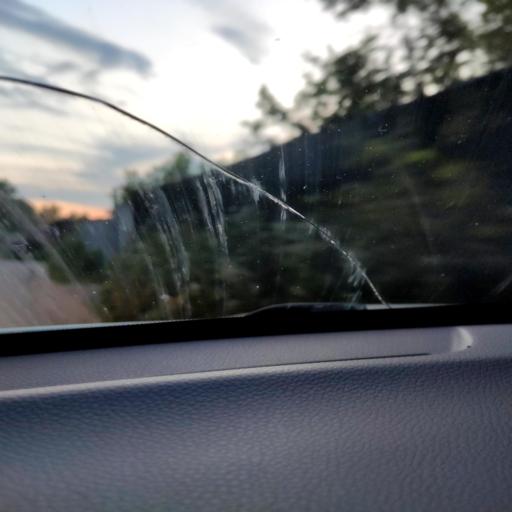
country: RU
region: Tatarstan
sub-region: Gorod Kazan'
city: Kazan
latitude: 55.8472
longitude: 49.1701
